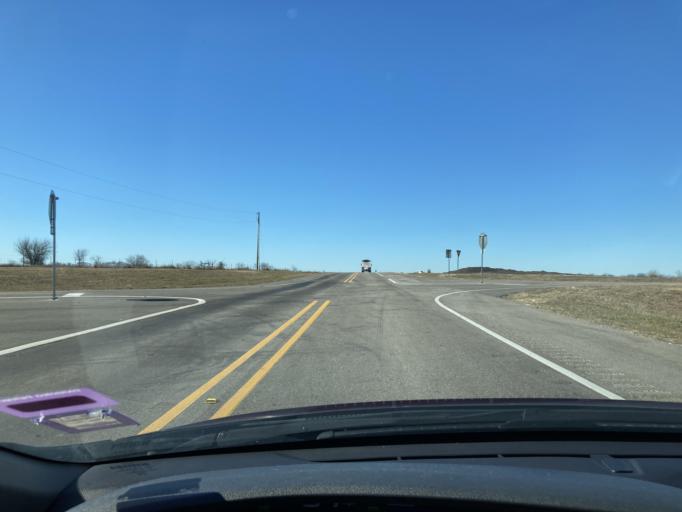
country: US
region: Texas
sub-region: Navarro County
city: Corsicana
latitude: 32.0480
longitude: -96.4813
